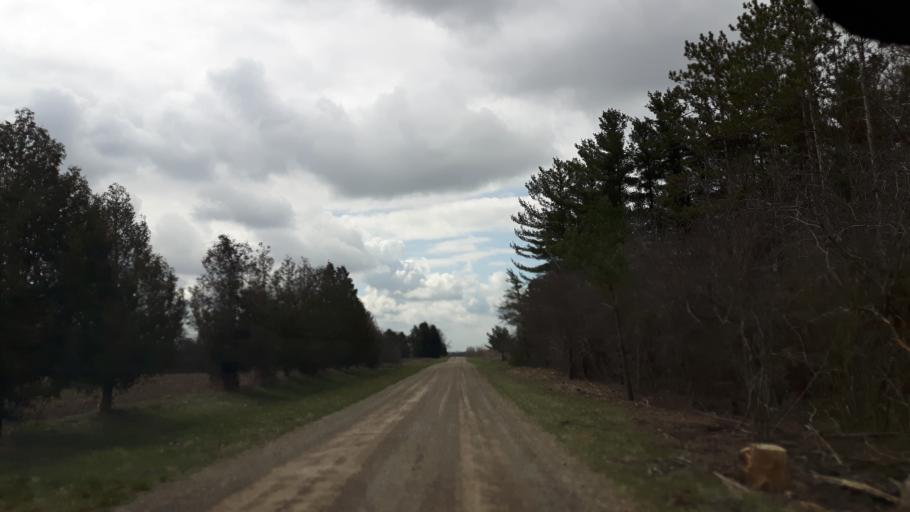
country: CA
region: Ontario
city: Bluewater
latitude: 43.5499
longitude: -81.6802
